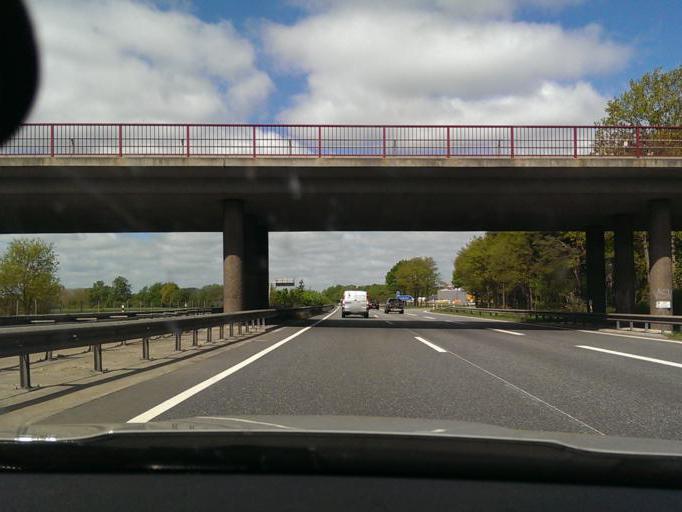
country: DE
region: Lower Saxony
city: Achim
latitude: 53.0189
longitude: 9.0658
